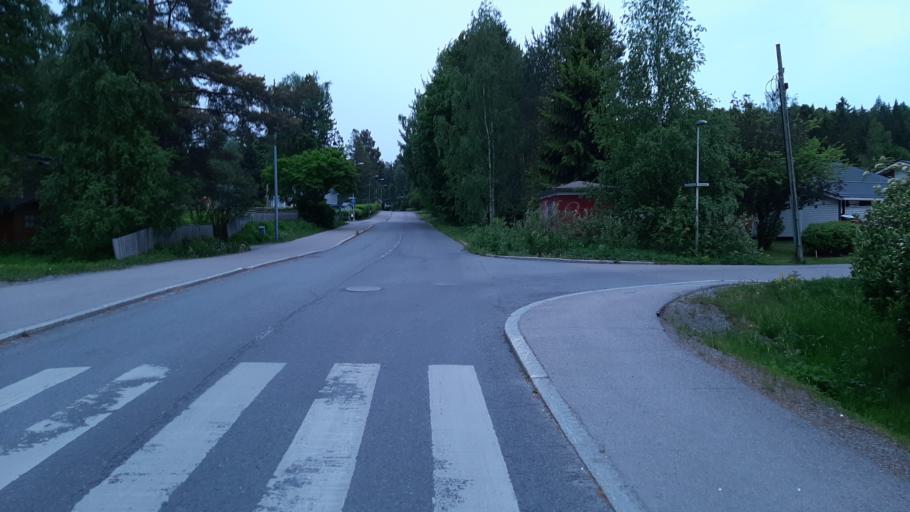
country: FI
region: Pirkanmaa
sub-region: Tampere
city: Tampere
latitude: 61.4732
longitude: 23.8261
